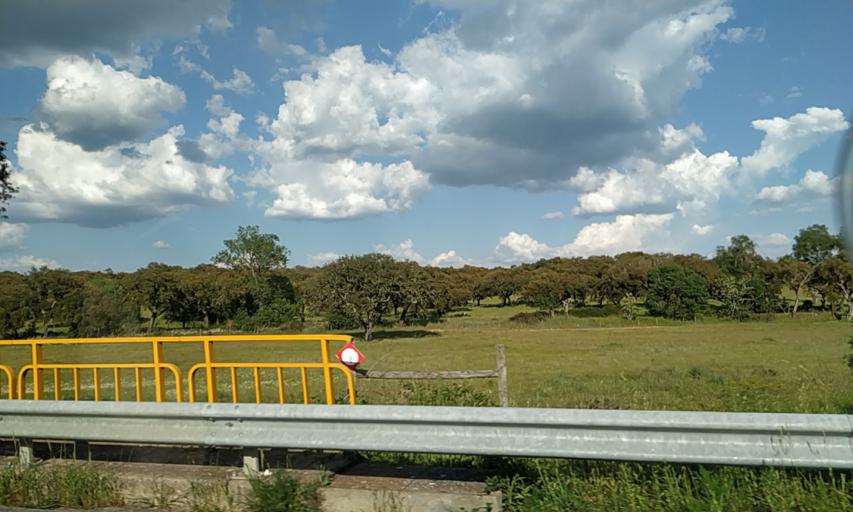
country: PT
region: Portalegre
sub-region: Portalegre
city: Urra
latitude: 39.2188
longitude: -7.4580
